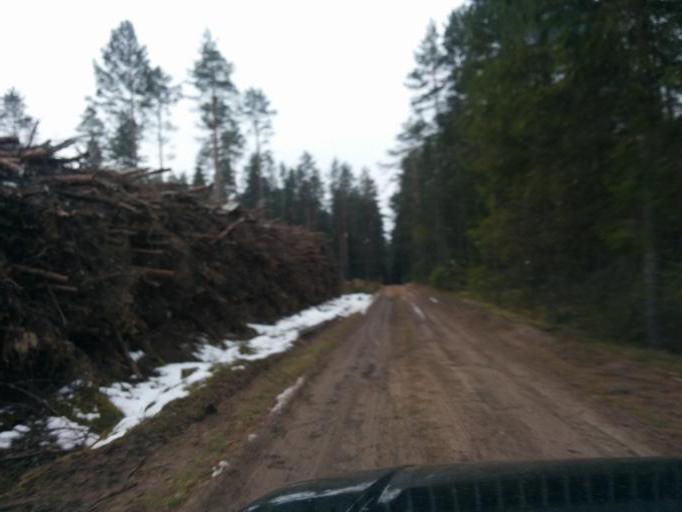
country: LV
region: Ikskile
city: Ikskile
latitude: 56.8039
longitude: 24.4833
